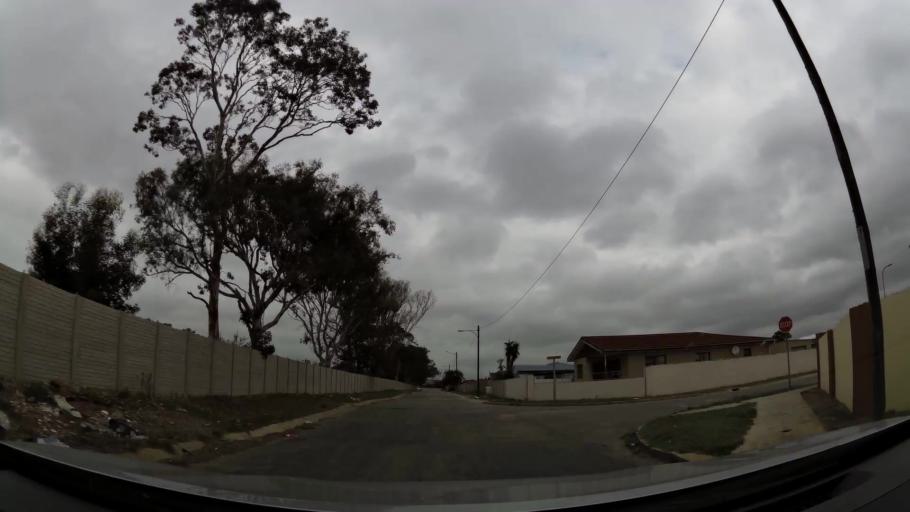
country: ZA
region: Eastern Cape
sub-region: Nelson Mandela Bay Metropolitan Municipality
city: Port Elizabeth
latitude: -33.9025
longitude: 25.5666
